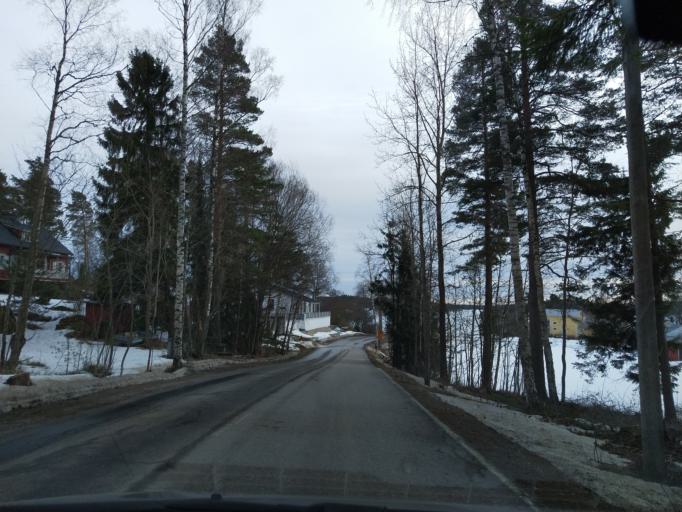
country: FI
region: Uusimaa
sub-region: Helsinki
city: Sibbo
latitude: 60.2574
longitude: 25.2909
